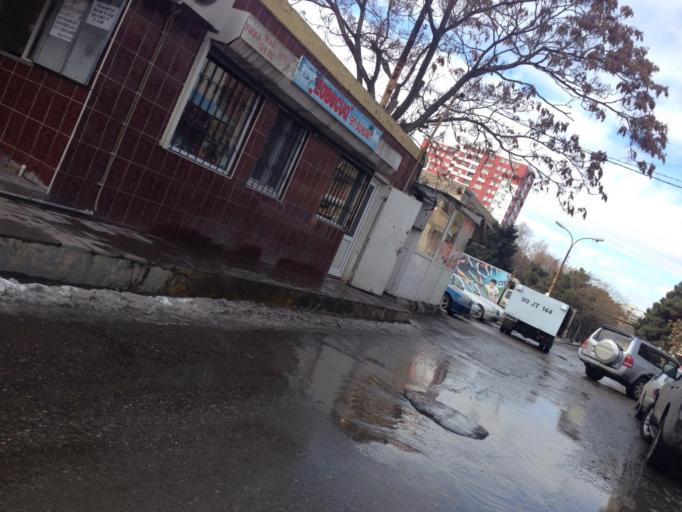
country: AZ
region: Baki
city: Baku
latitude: 40.3934
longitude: 49.8772
